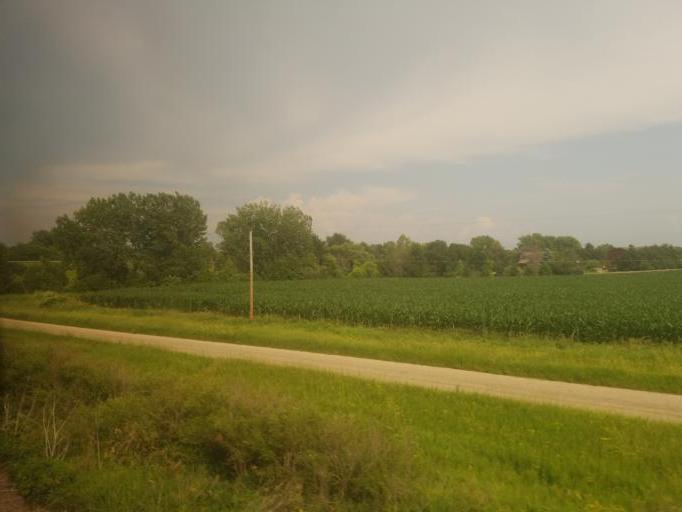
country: US
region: Illinois
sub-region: Bureau County
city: Princeton
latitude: 41.3196
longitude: -89.6870
